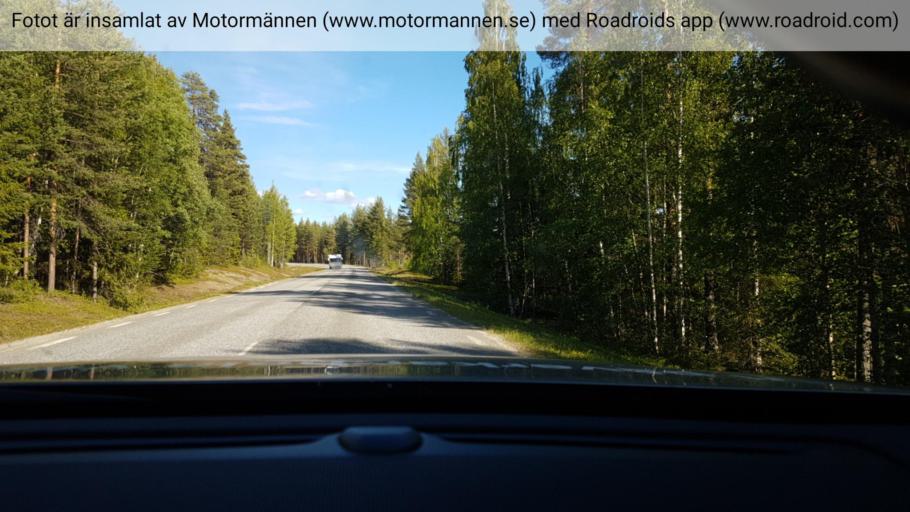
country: SE
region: Vaesterbotten
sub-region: Lycksele Kommun
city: Lycksele
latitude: 64.8203
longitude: 18.8413
